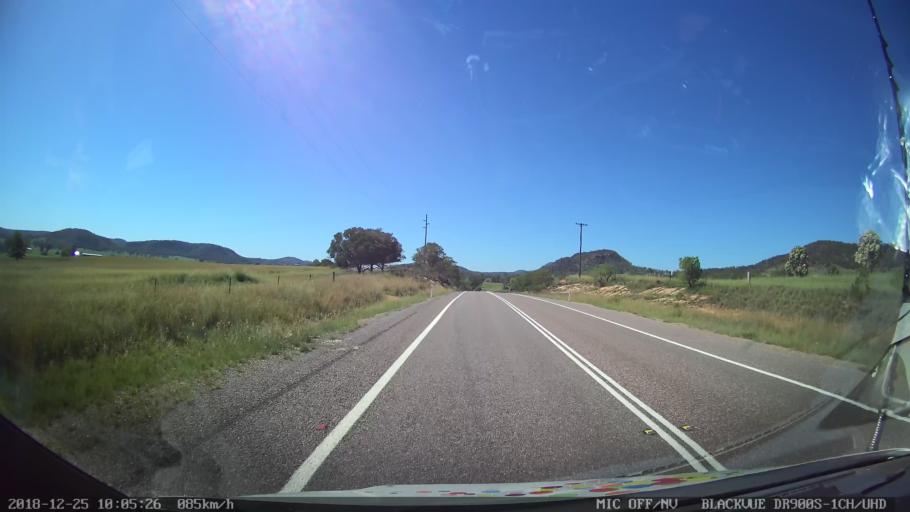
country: AU
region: New South Wales
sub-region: Upper Hunter Shire
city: Merriwa
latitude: -32.2471
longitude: 150.4863
